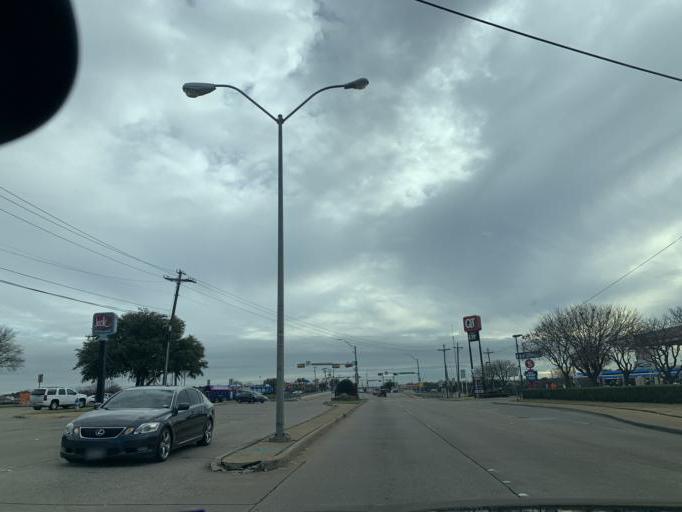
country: US
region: Texas
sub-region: Dallas County
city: Duncanville
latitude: 32.6430
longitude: -96.8915
